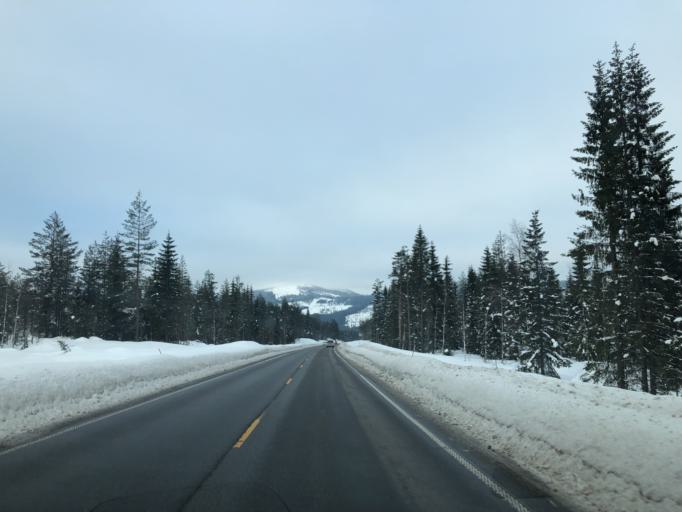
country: NO
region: Hedmark
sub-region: Trysil
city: Innbygda
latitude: 61.2527
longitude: 12.2993
